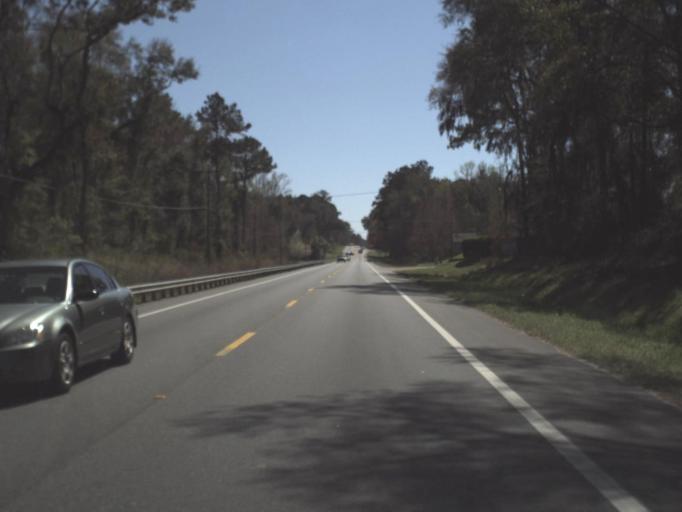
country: US
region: Florida
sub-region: Gadsden County
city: Midway
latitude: 30.5067
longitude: -84.3620
